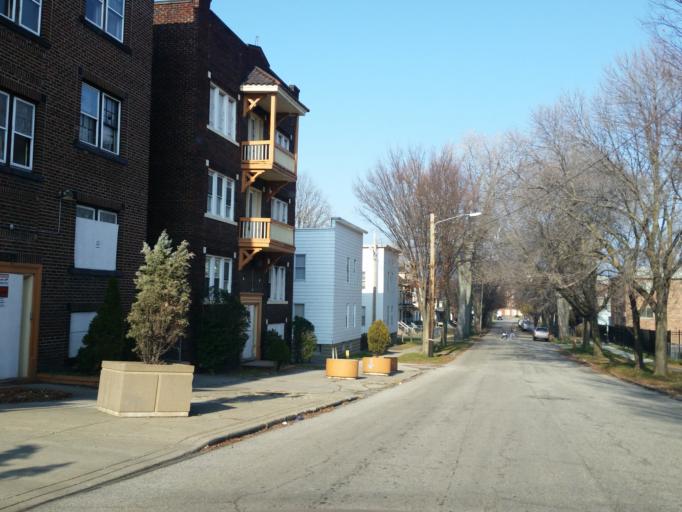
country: US
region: Ohio
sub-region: Cuyahoga County
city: Brooklyn
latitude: 41.4814
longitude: -81.7416
